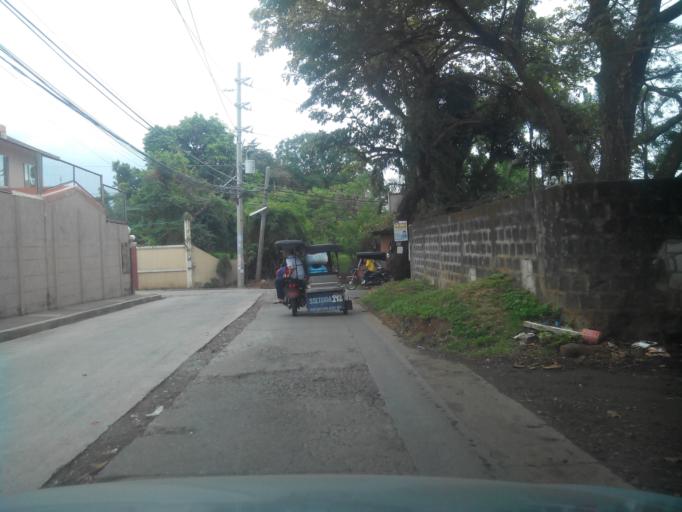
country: PH
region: Calabarzon
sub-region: Province of Rizal
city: Teresa
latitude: 14.5942
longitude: 121.1808
